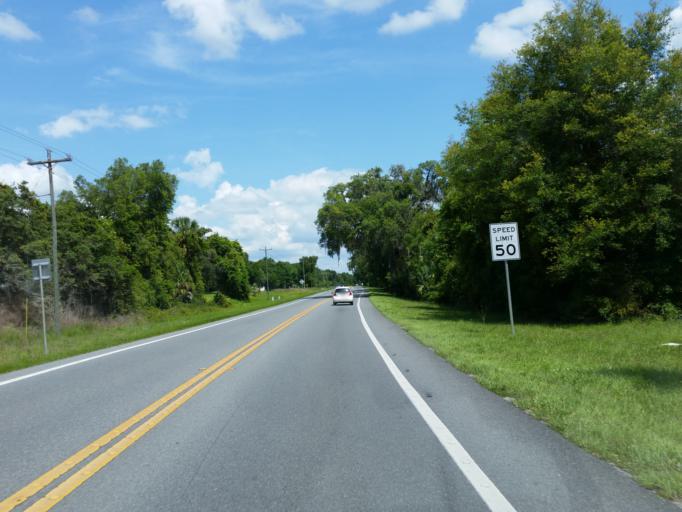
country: US
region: Florida
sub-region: Citrus County
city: Inverness Highlands North
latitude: 28.8667
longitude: -82.3584
